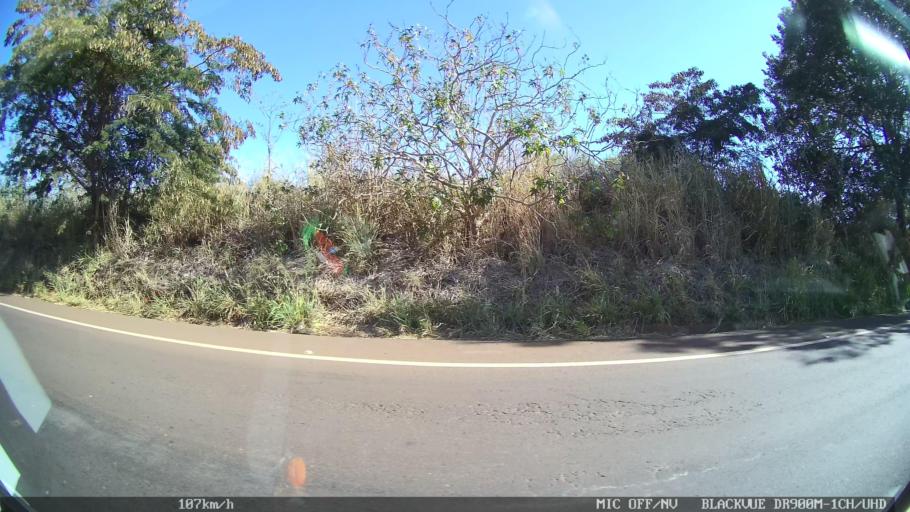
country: BR
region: Sao Paulo
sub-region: Olimpia
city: Olimpia
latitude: -20.7236
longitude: -48.8673
